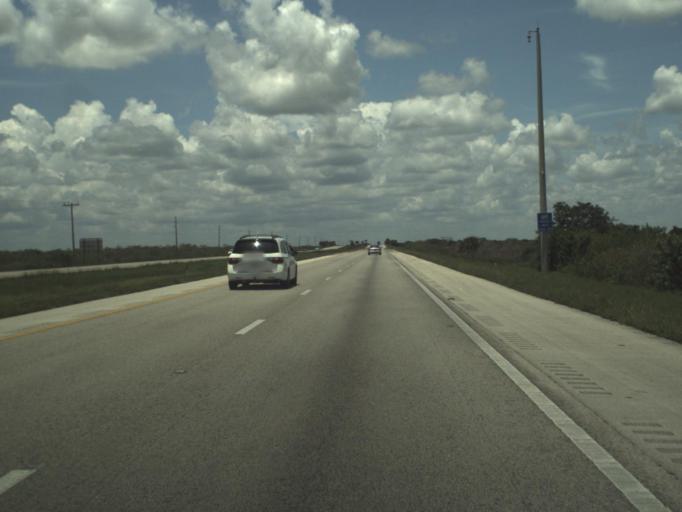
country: US
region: Florida
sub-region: Broward County
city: Weston
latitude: 26.1551
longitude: -80.7541
